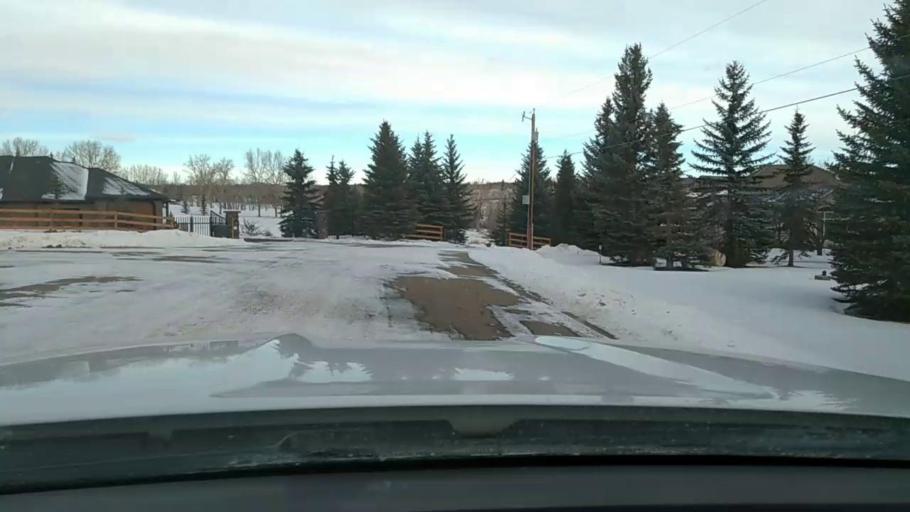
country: CA
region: Alberta
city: Cochrane
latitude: 51.1527
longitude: -114.2697
